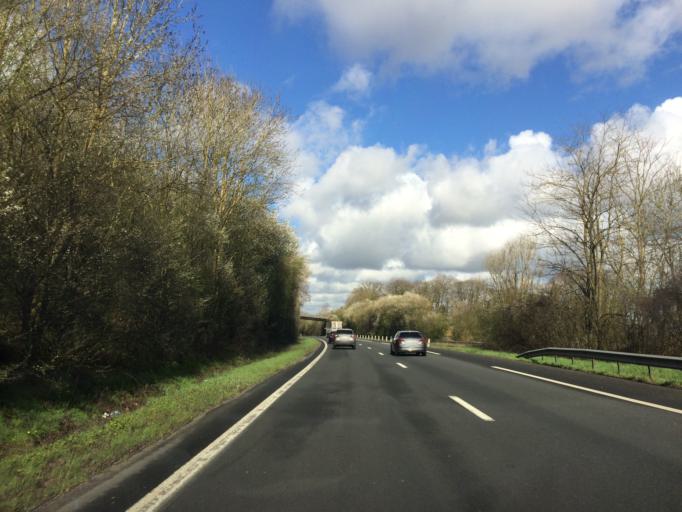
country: FR
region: Ile-de-France
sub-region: Departement de l'Essonne
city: Marcoussis
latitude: 48.6433
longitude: 2.1976
